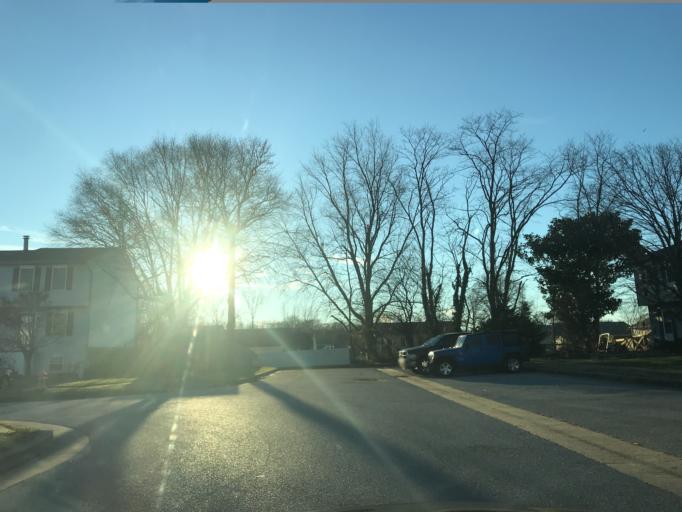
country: US
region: Maryland
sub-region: Baltimore County
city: Bowleys Quarters
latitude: 39.3296
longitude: -76.3857
